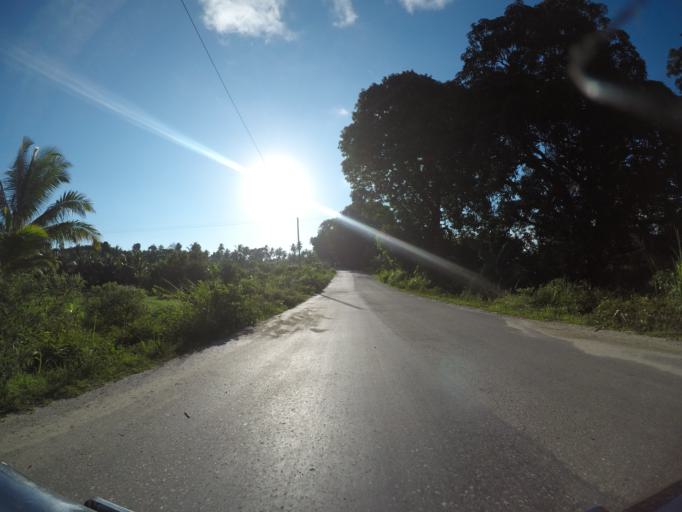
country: TZ
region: Pemba South
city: Mtambile
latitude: -5.3681
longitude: 39.7112
